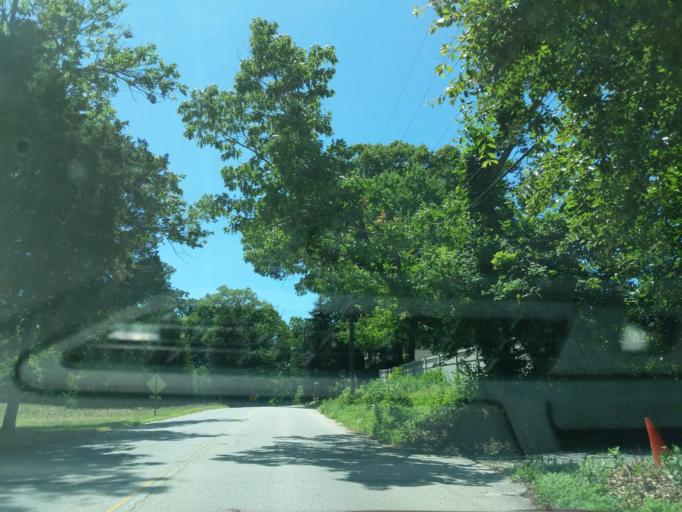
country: US
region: New Jersey
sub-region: Gloucester County
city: Wenonah
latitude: 39.7999
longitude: -75.1366
